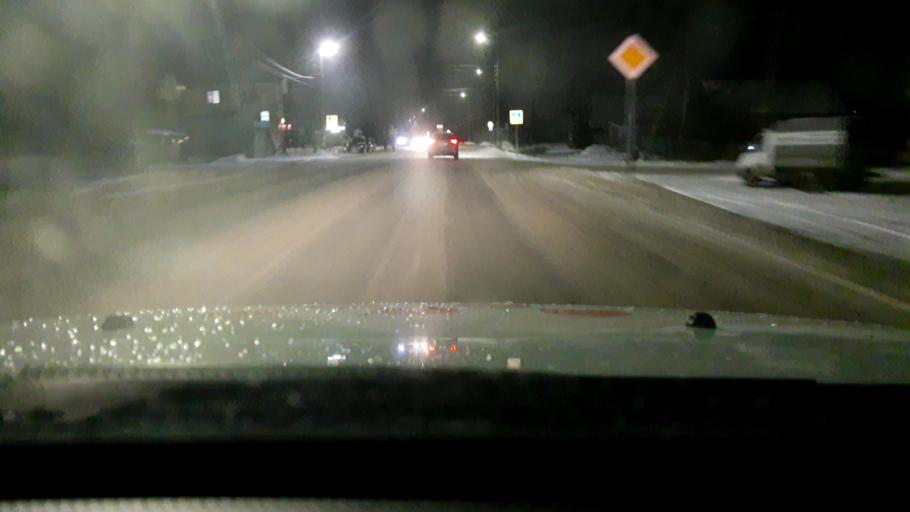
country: RU
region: Nizjnij Novgorod
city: Gorodets
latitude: 56.6626
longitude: 43.4692
